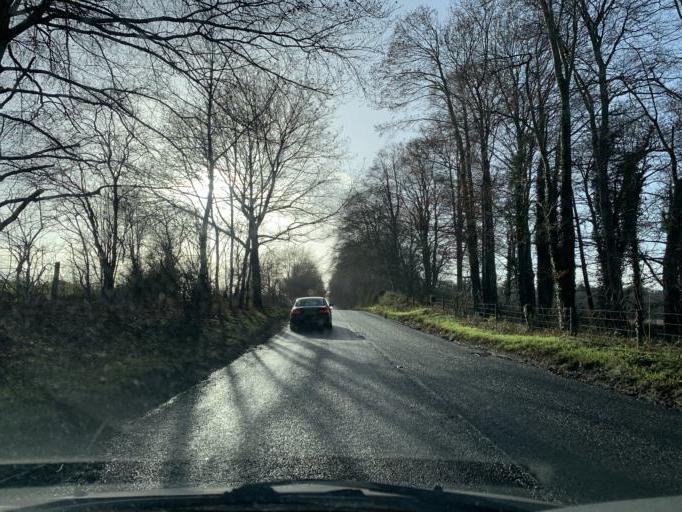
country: GB
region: England
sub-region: Wiltshire
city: Winterbourne Stoke
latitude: 51.1615
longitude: -1.8591
